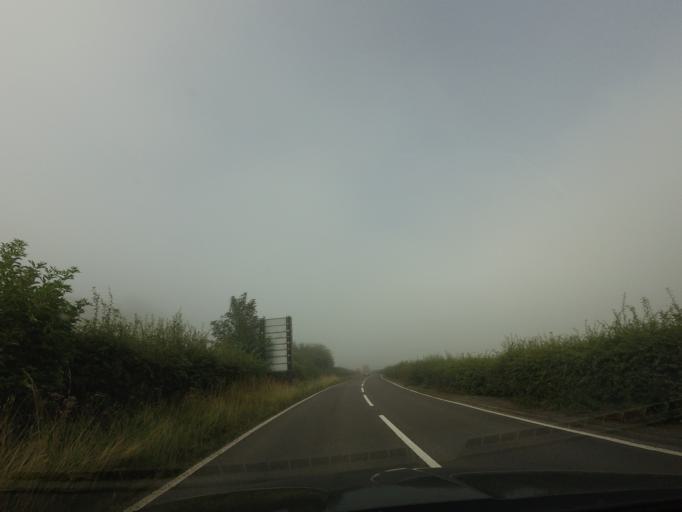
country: GB
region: England
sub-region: Derbyshire
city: Bakewell
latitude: 53.2287
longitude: -1.6627
